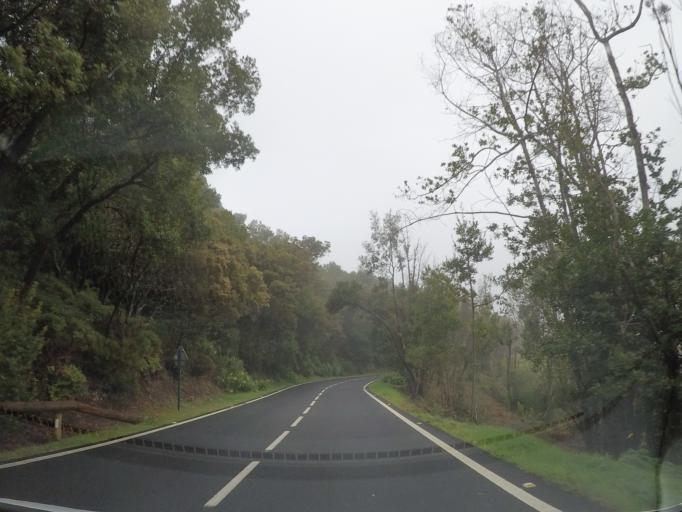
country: ES
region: Canary Islands
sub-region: Provincia de Santa Cruz de Tenerife
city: Alajero
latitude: 28.1200
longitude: -17.2483
